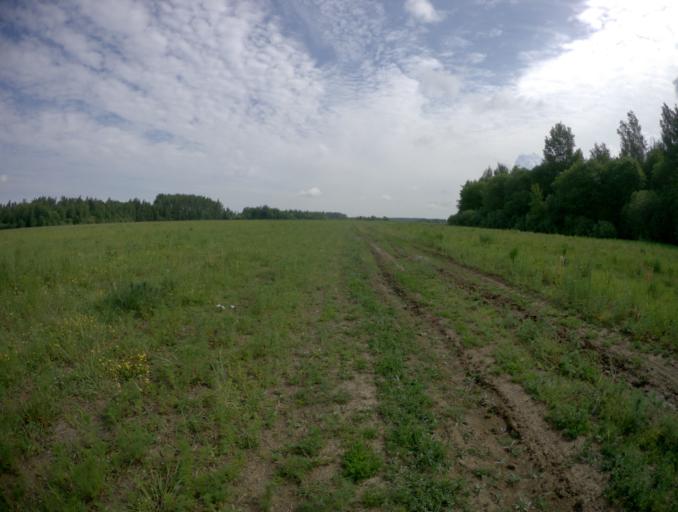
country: RU
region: Vladimir
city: Lakinsk
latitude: 56.0942
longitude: 39.9078
